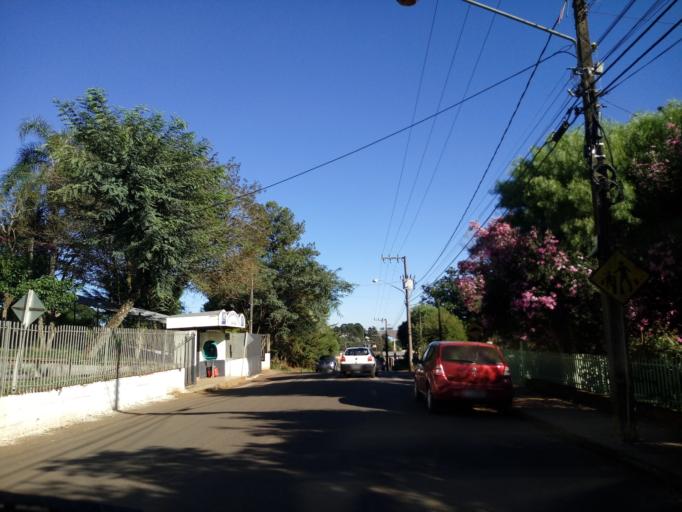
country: BR
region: Santa Catarina
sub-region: Chapeco
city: Chapeco
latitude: -27.1923
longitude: -52.6484
